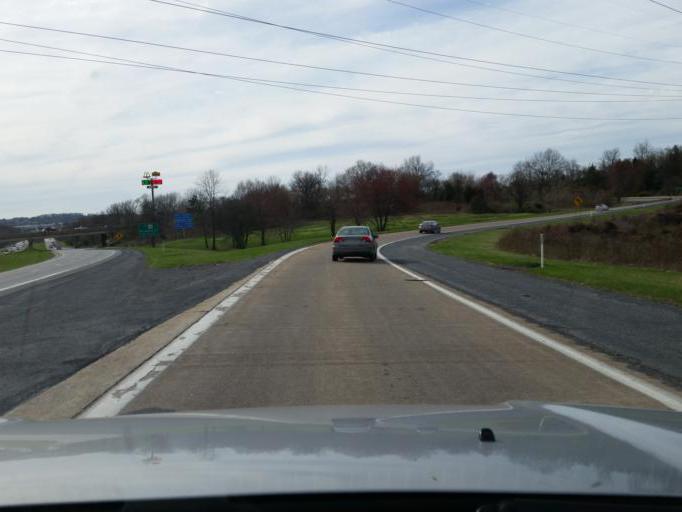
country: US
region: Pennsylvania
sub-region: Dauphin County
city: Middletown
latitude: 40.2238
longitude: -76.7153
